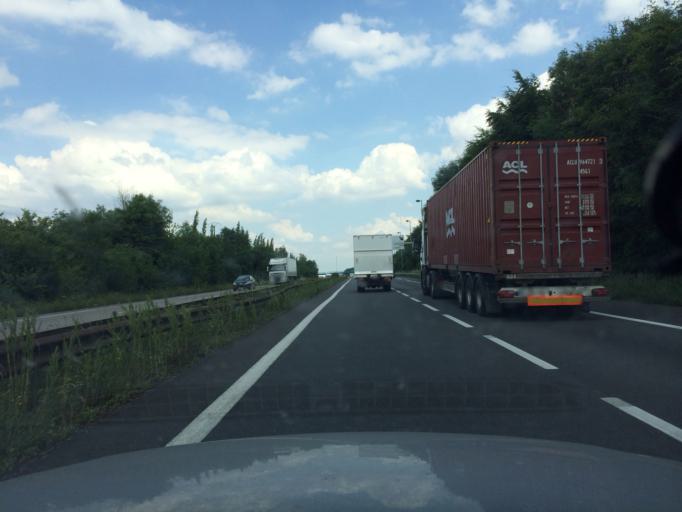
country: FR
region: Lorraine
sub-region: Departement de Meurthe-et-Moselle
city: Velaine-en-Haye
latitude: 48.6924
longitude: 6.0646
